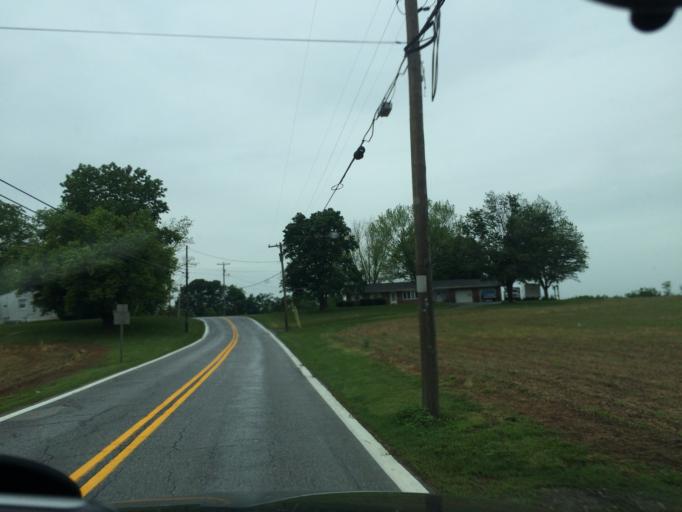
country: US
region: Maryland
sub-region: Carroll County
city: Taneytown
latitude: 39.6033
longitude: -77.2387
